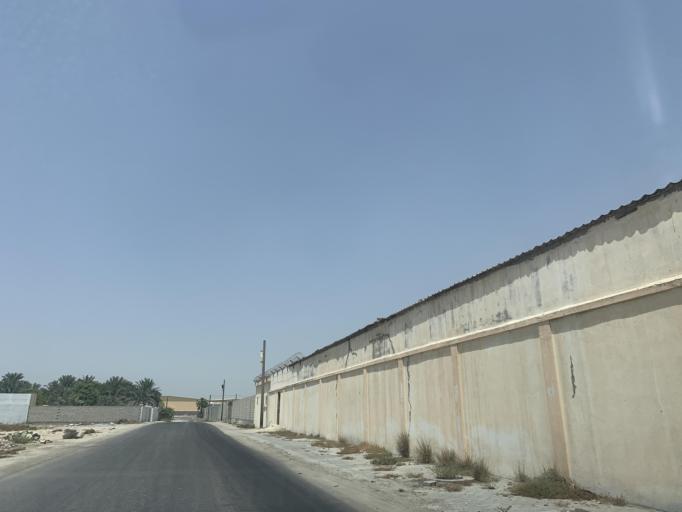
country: BH
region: Central Governorate
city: Madinat Hamad
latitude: 26.1586
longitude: 50.4899
